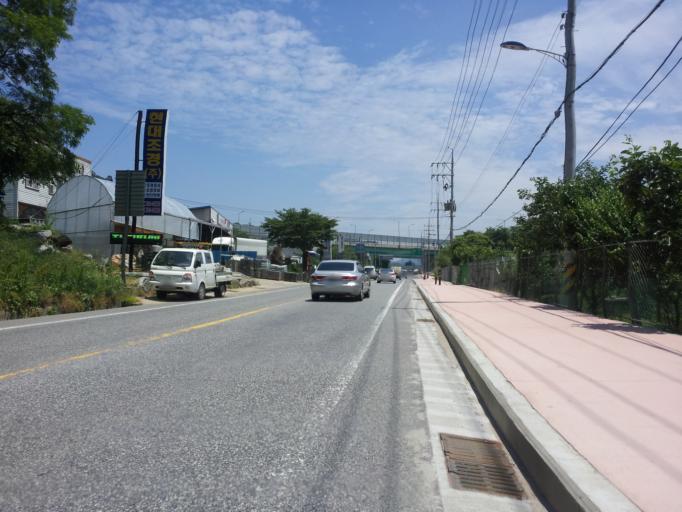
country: KR
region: Chungcheongbuk-do
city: Okcheon
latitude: 36.3110
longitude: 127.5648
